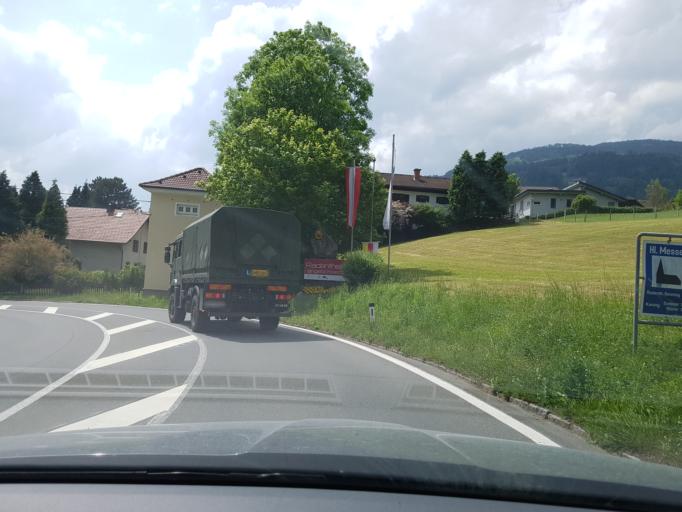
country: AT
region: Carinthia
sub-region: Politischer Bezirk Spittal an der Drau
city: Radenthein
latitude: 46.8017
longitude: 13.7105
